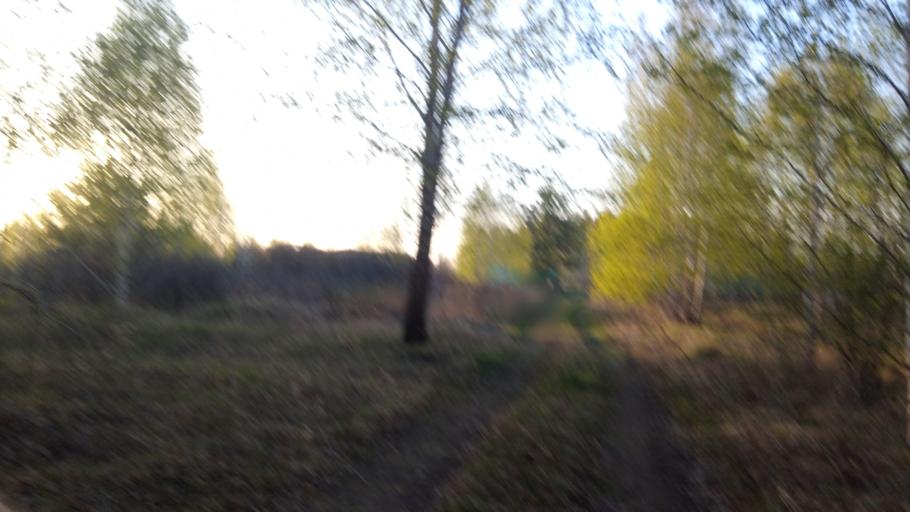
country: RU
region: Chelyabinsk
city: Timiryazevskiy
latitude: 54.9928
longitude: 60.8513
